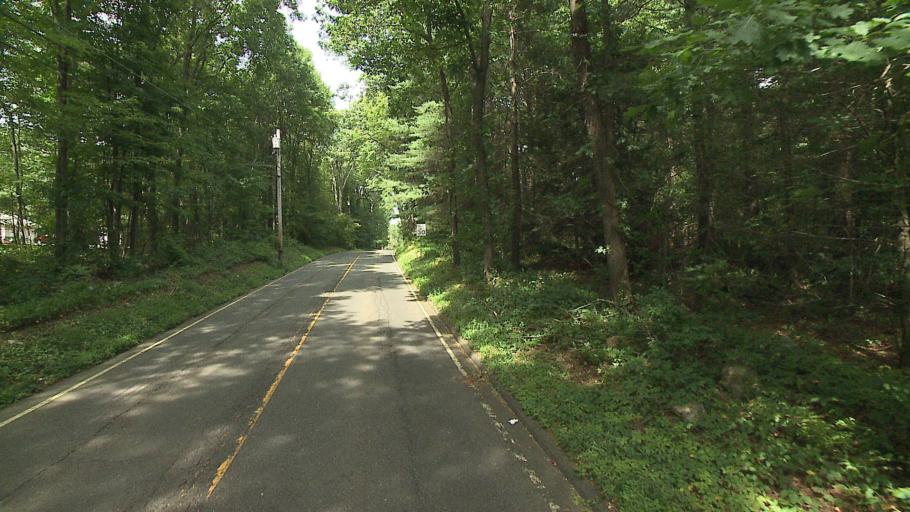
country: US
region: Connecticut
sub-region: Litchfield County
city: Bethlehem Village
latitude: 41.6452
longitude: -73.1652
